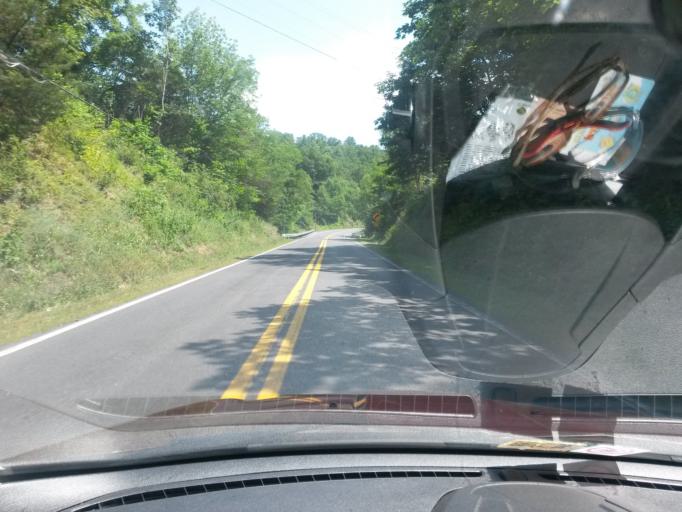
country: US
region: West Virginia
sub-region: Pendleton County
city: Franklin
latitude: 38.6698
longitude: -79.3295
